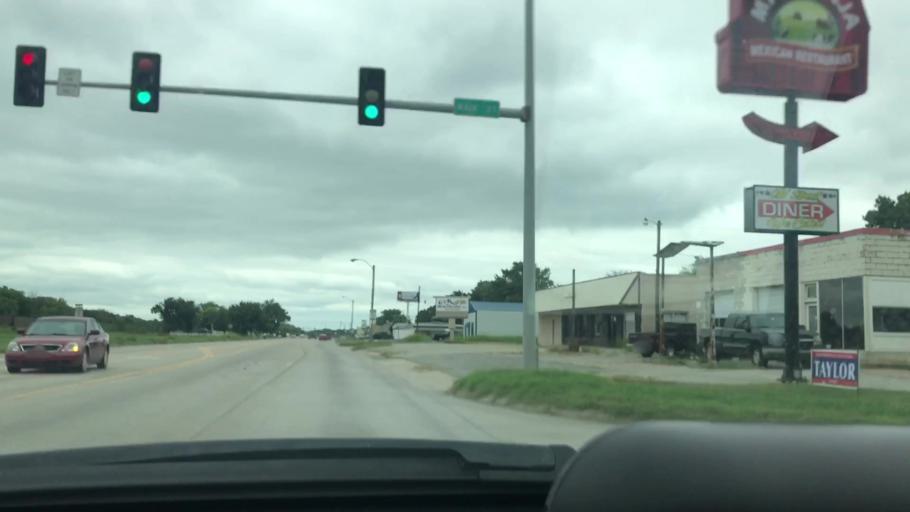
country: US
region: Oklahoma
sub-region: Mayes County
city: Chouteau
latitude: 36.1864
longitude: -95.3426
